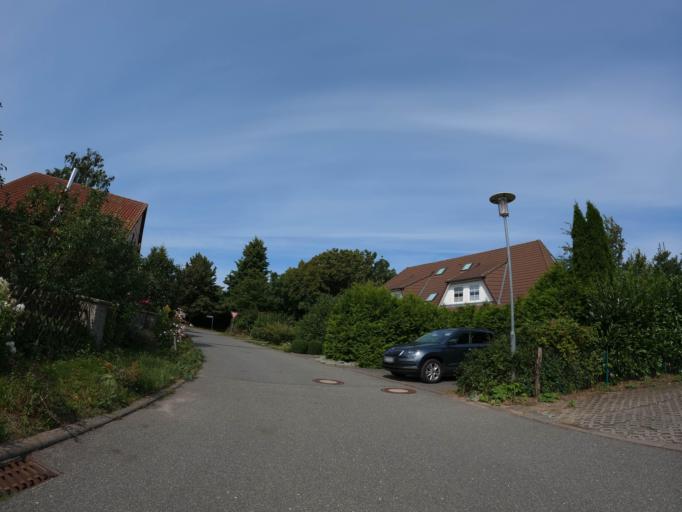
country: DE
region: Mecklenburg-Vorpommern
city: Altefahr
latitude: 54.3322
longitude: 13.1333
